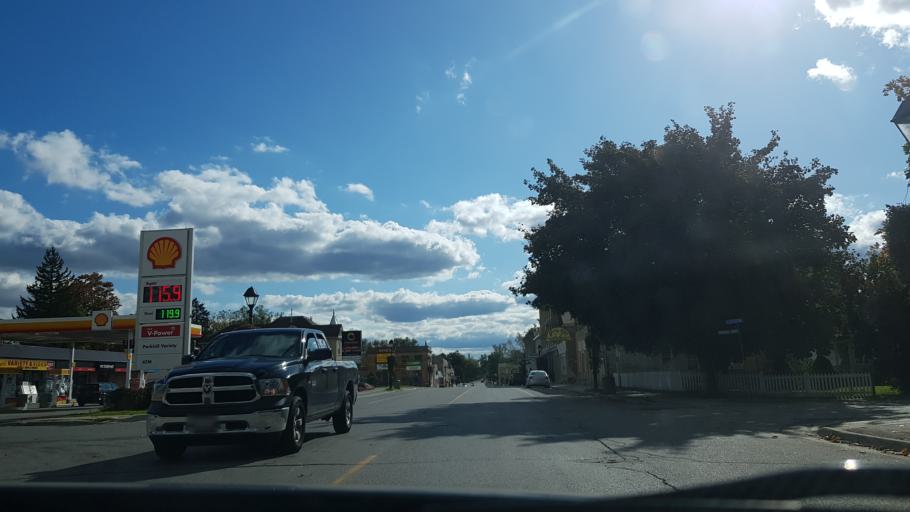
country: CA
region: Ontario
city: South Huron
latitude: 43.1650
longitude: -81.6834
